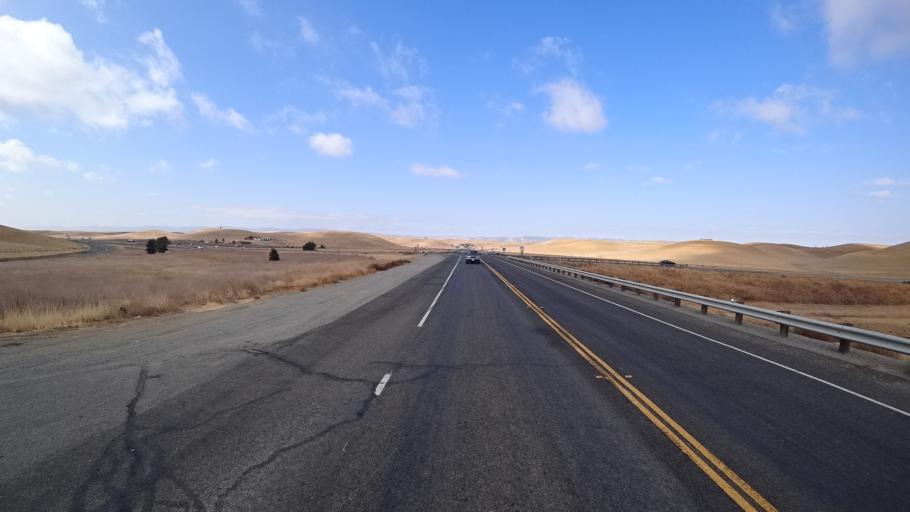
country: US
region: California
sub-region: Yolo County
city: Dunnigan
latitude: 38.7773
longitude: -121.9437
